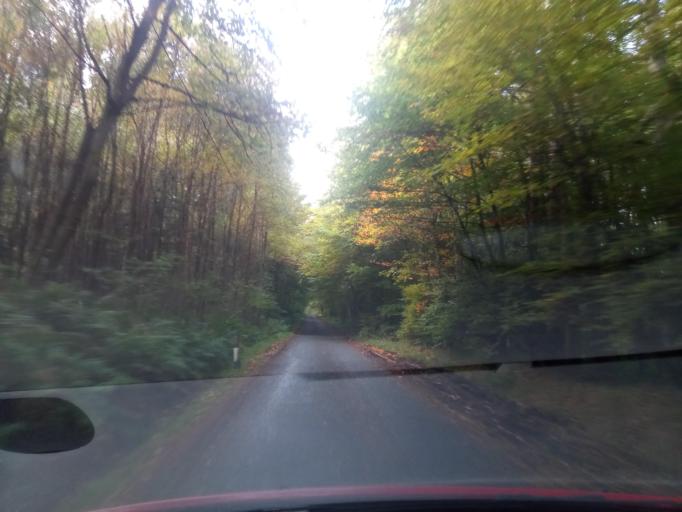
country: GB
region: Scotland
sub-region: The Scottish Borders
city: Galashiels
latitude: 55.6694
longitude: -2.8007
